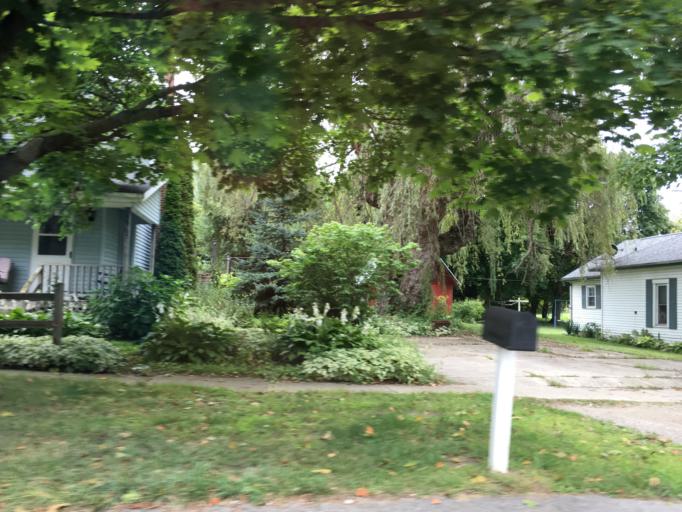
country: US
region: Michigan
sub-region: Tuscola County
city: Caro
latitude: 43.3378
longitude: -83.3514
